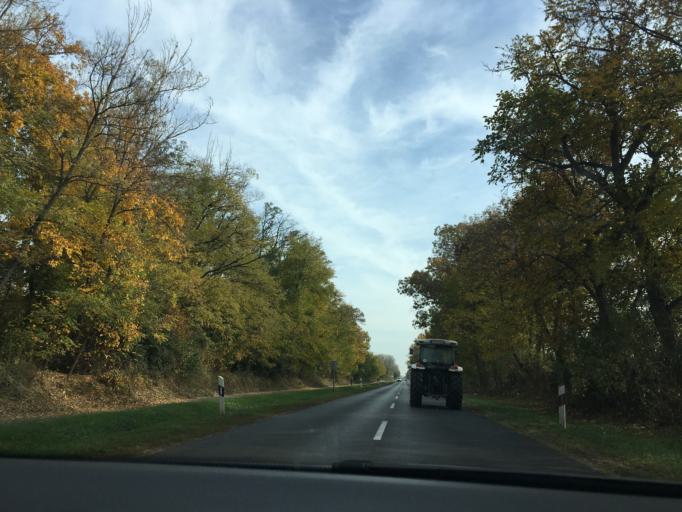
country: HU
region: Szabolcs-Szatmar-Bereg
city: Nagykallo
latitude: 47.8685
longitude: 21.8745
